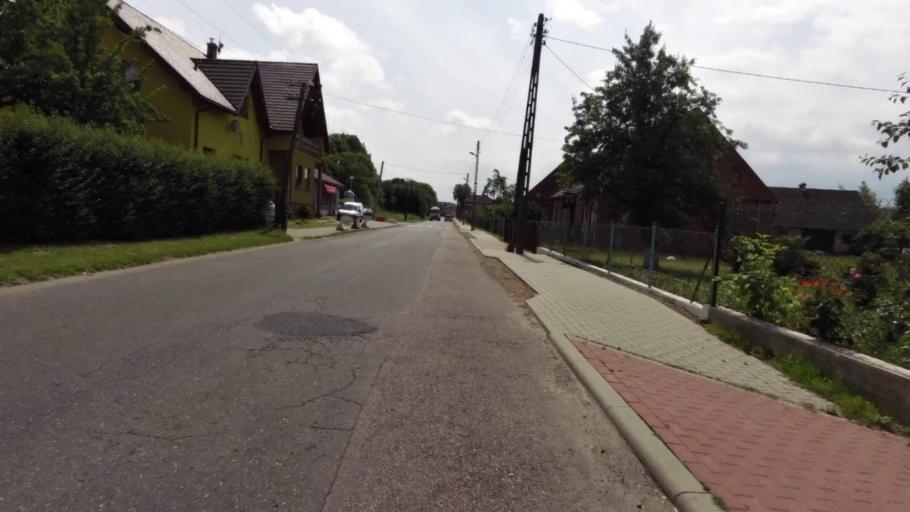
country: PL
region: West Pomeranian Voivodeship
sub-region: Powiat goleniowski
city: Stepnica
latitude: 53.7328
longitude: 14.6620
